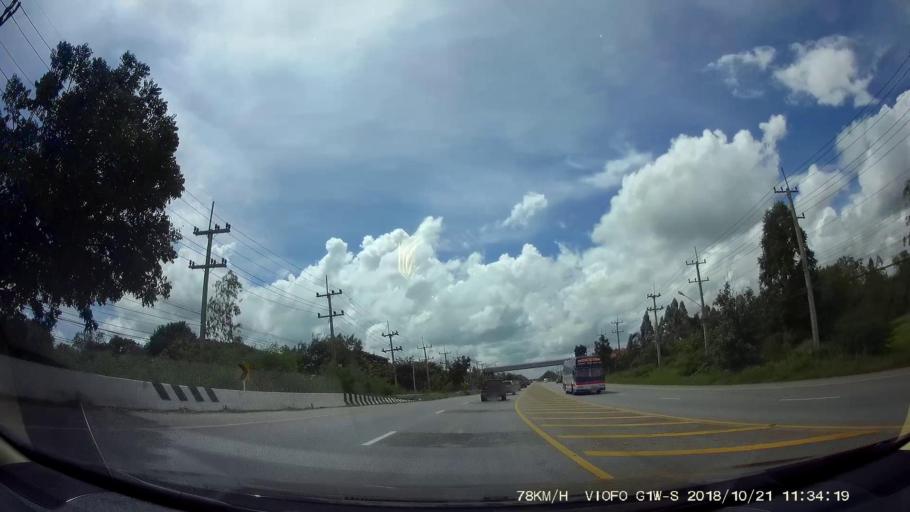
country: TH
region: Chaiyaphum
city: Chaiyaphum
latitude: 15.7333
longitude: 102.0242
